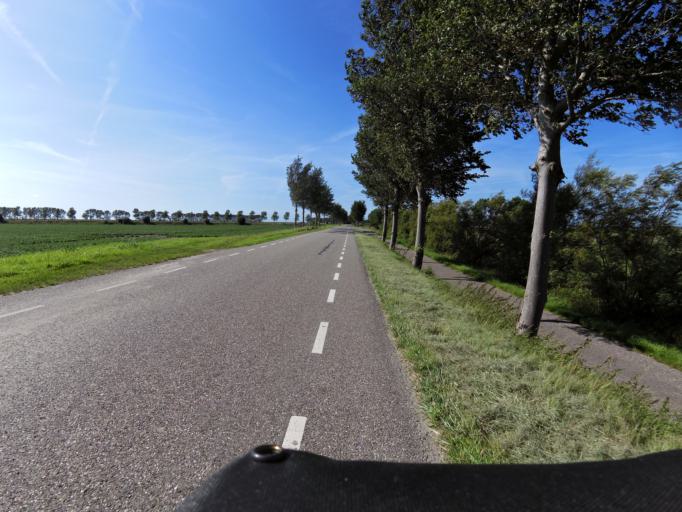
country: NL
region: South Holland
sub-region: Gemeente Goeree-Overflakkee
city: Dirksland
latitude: 51.7310
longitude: 4.0724
